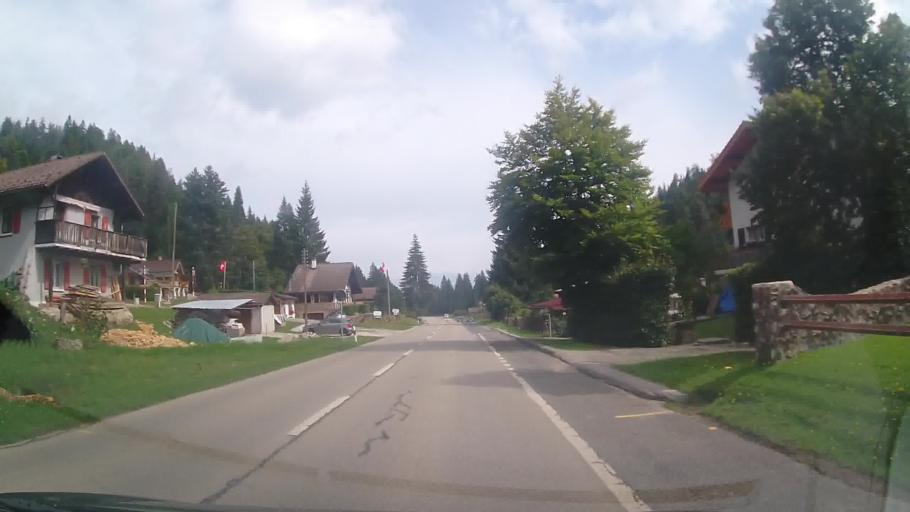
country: CH
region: Vaud
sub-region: Nyon District
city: Saint-Cergue
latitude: 46.4540
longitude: 6.1180
